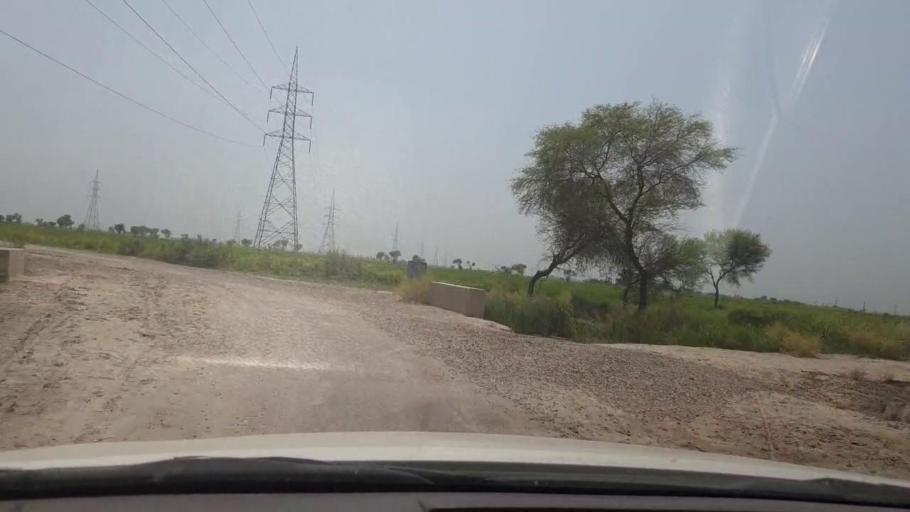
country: PK
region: Sindh
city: Shikarpur
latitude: 28.0922
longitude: 68.6178
